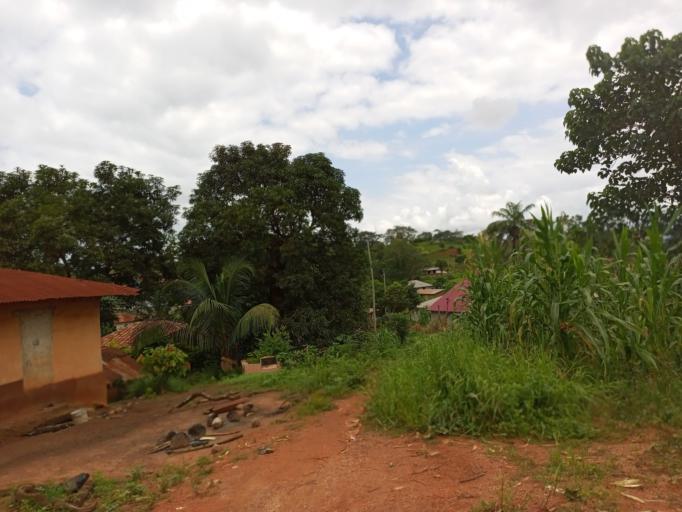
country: SL
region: Northern Province
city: Kamakwie
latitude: 9.4999
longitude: -12.2483
